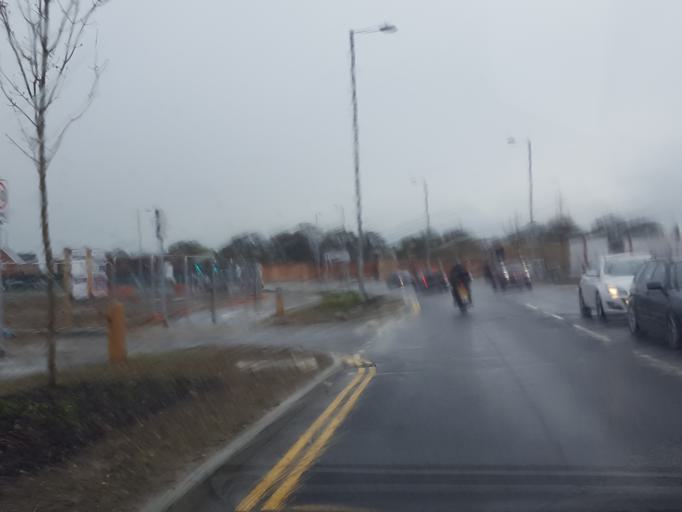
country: GB
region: England
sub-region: Essex
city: Great Horkesley
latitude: 51.9188
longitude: 0.8880
